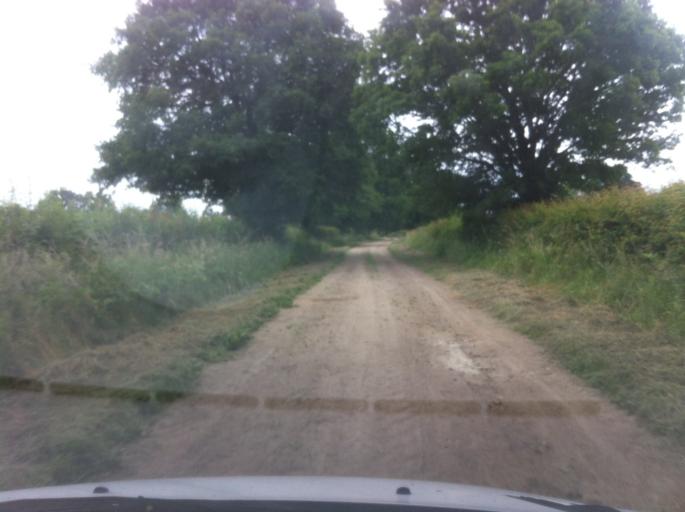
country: FR
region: Auvergne
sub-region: Departement de l'Allier
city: Chantelle
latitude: 46.3250
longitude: 3.1067
